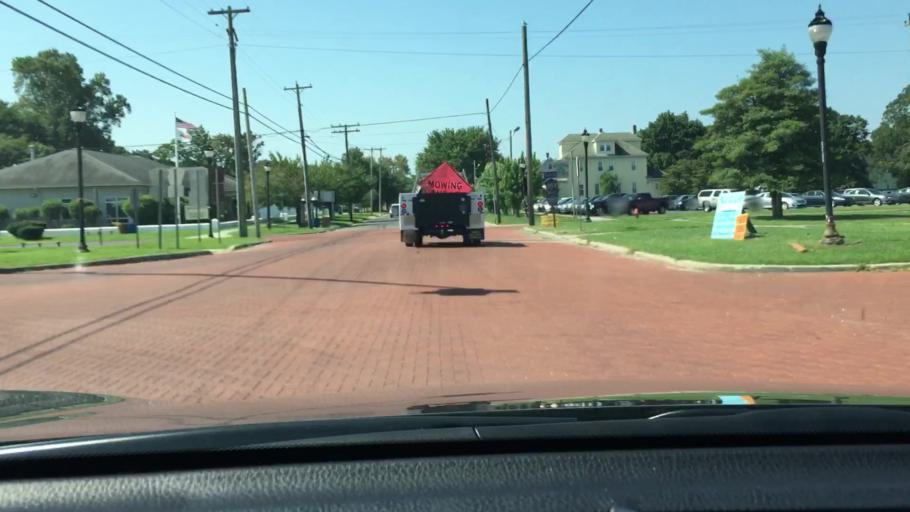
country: US
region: New Jersey
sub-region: Cape May County
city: Woodbine
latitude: 39.2419
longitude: -74.8154
